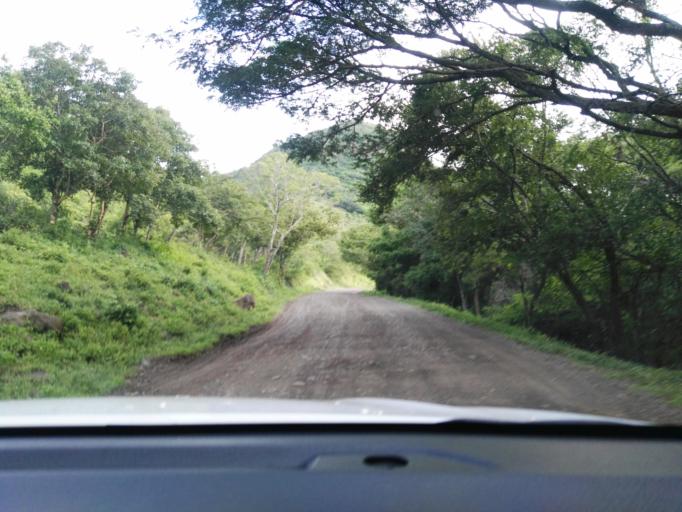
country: NI
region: Matagalpa
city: Ciudad Dario
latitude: 12.8470
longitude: -86.0479
